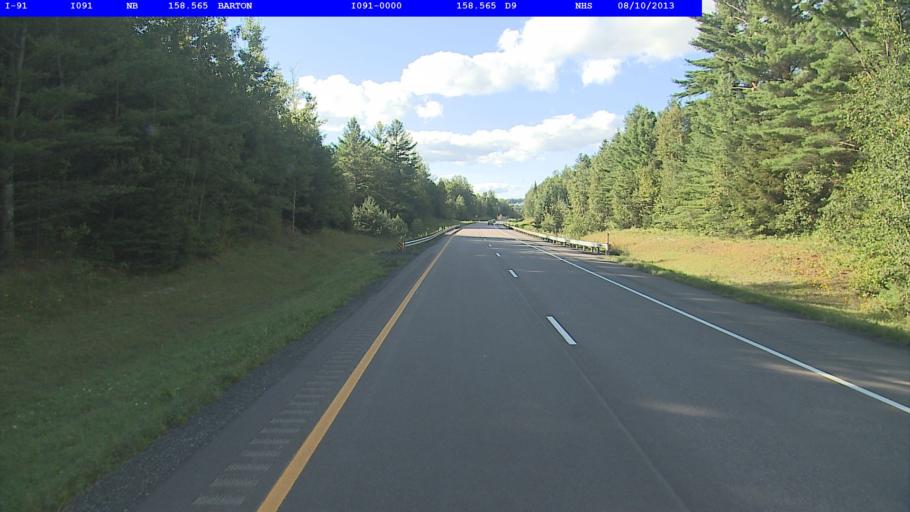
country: US
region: Vermont
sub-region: Orleans County
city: Newport
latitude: 44.7660
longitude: -72.2109
